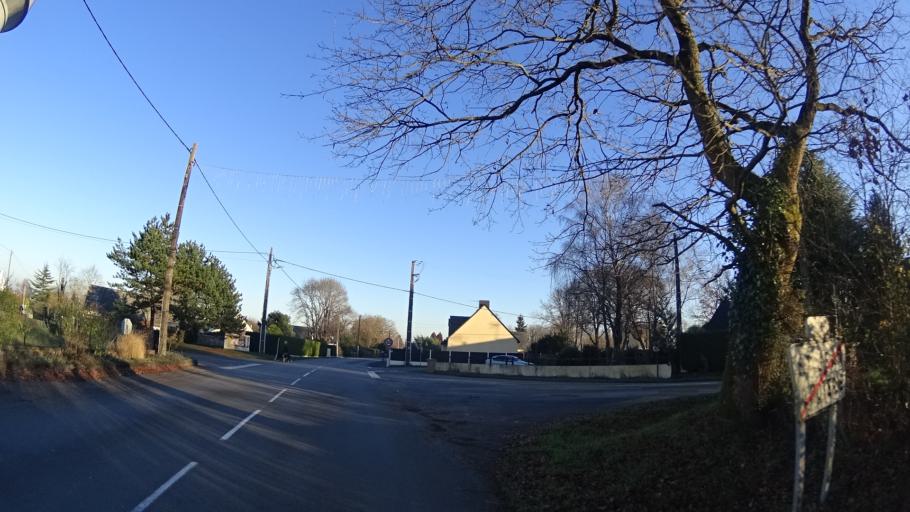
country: FR
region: Brittany
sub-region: Departement du Morbihan
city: Saint-Jean-la-Poterie
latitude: 47.6350
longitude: -2.1141
